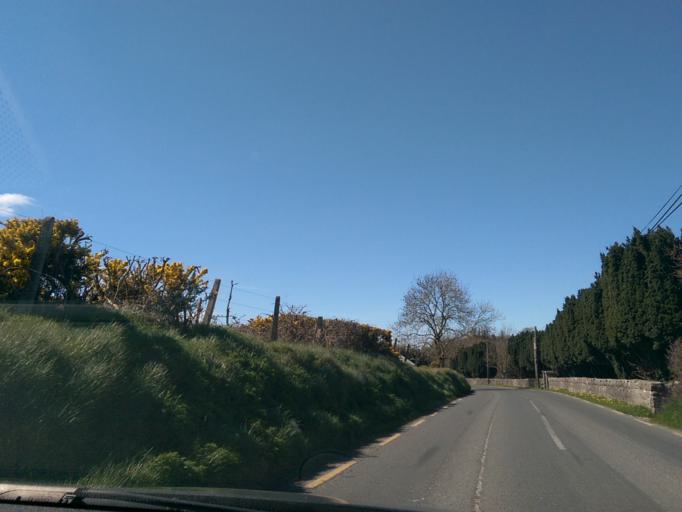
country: IE
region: Leinster
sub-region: Wicklow
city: Baltinglass
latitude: 52.8995
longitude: -6.6049
